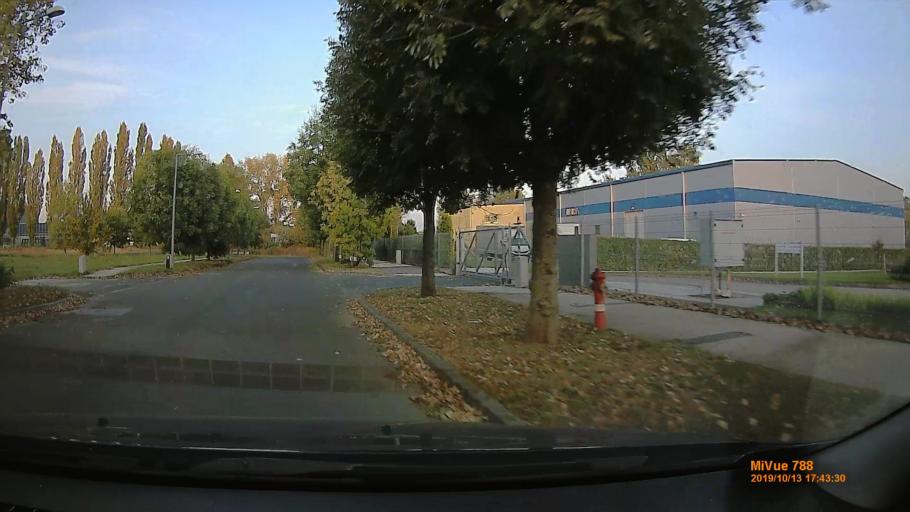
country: HU
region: Budapest
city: Budapest XVII. keruelet
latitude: 47.5022
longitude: 19.2173
